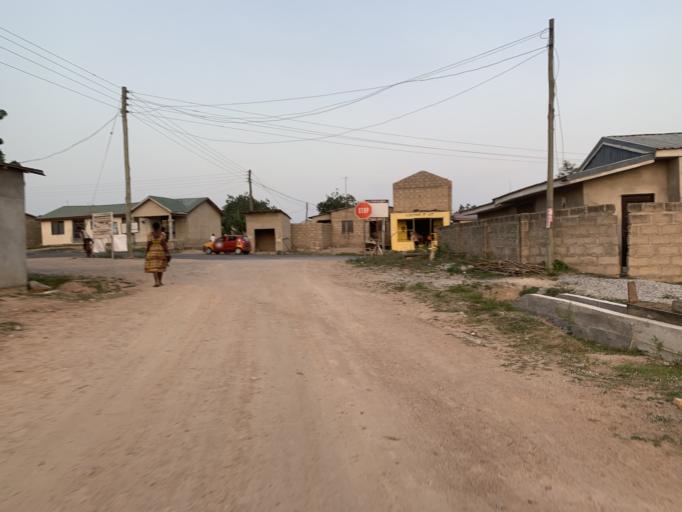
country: GH
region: Central
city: Winneba
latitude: 5.3757
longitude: -0.6069
